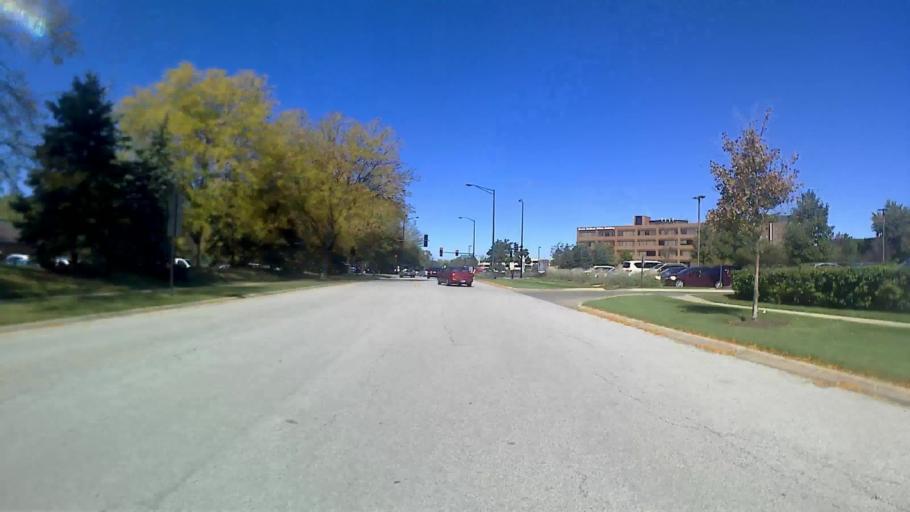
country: US
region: Illinois
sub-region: DuPage County
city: Itasca
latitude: 42.0024
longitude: -88.0183
